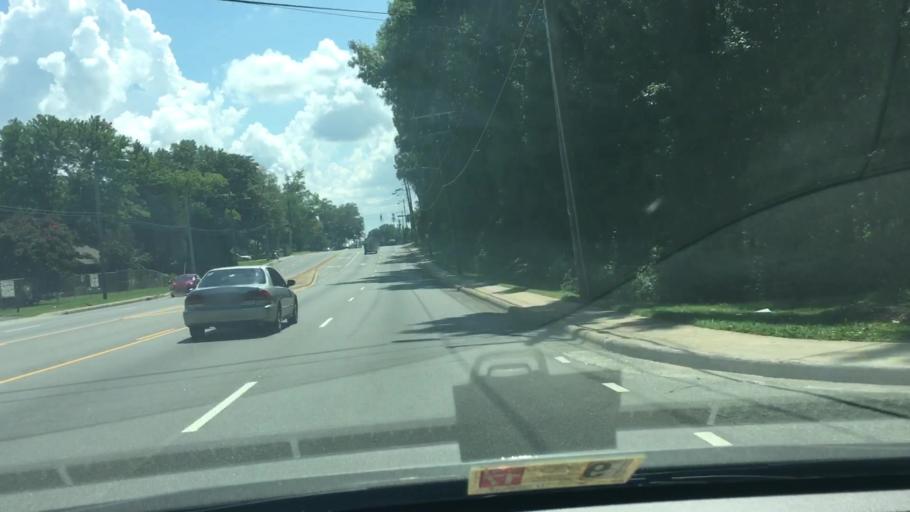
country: US
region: North Carolina
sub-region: Mecklenburg County
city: Charlotte
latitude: 35.2723
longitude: -80.7939
